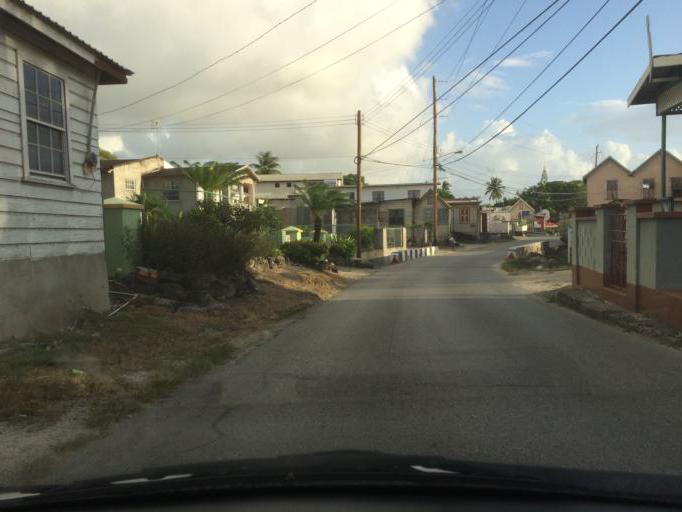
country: BB
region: Saint Lucy
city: Checker Hall
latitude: 13.2785
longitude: -59.6474
